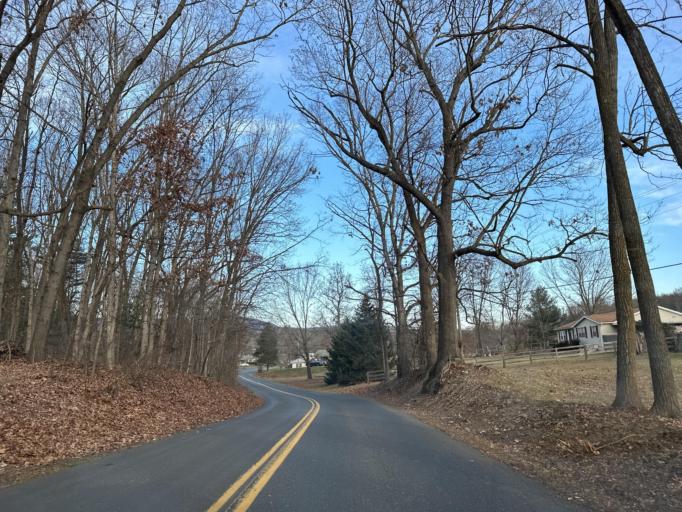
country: US
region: Virginia
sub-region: City of Staunton
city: Staunton
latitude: 38.2104
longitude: -79.2027
